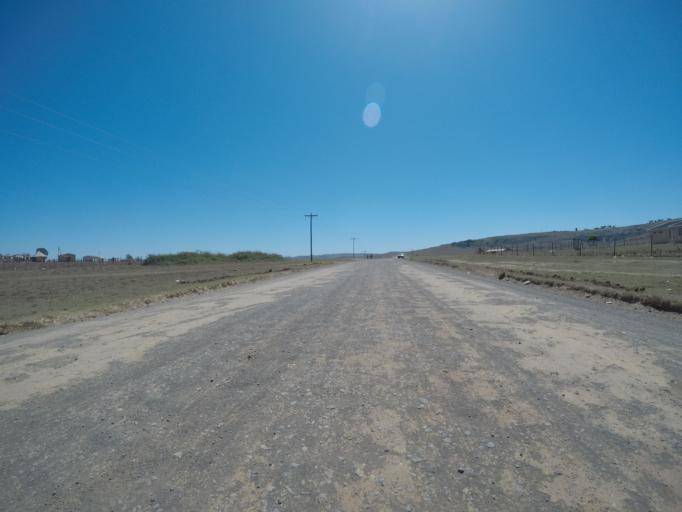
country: ZA
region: Eastern Cape
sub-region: OR Tambo District Municipality
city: Mthatha
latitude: -31.7835
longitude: 28.8073
